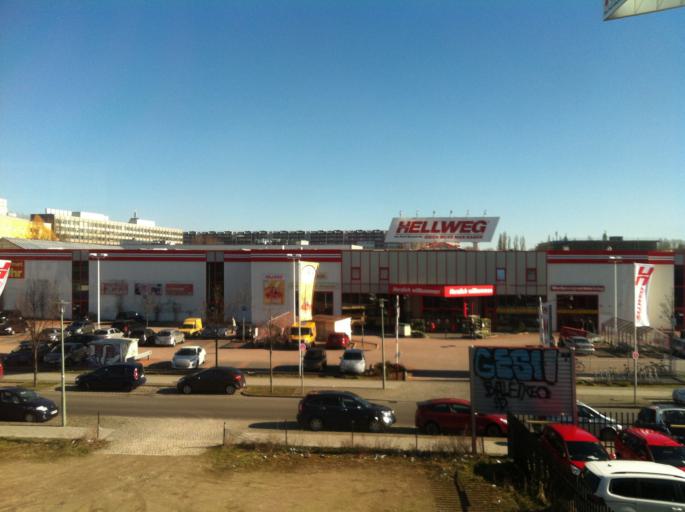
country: DE
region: Berlin
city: Berlin Treptow
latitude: 52.5091
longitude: 13.4394
